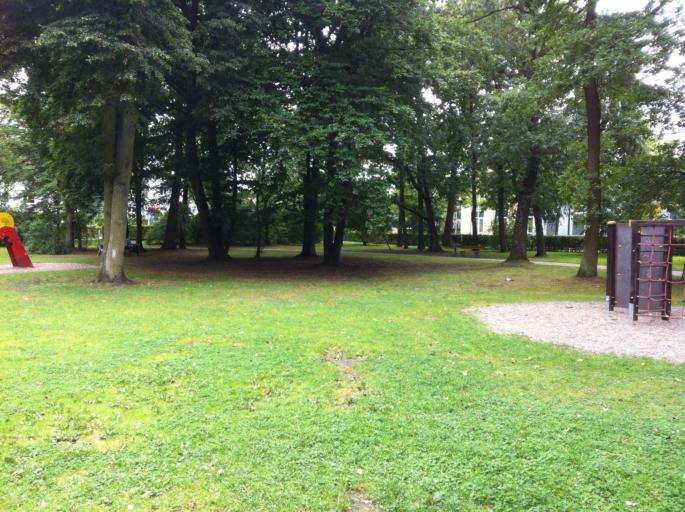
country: DE
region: Bavaria
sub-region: Upper Franconia
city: Bayreuth
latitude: 49.9378
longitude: 11.5814
